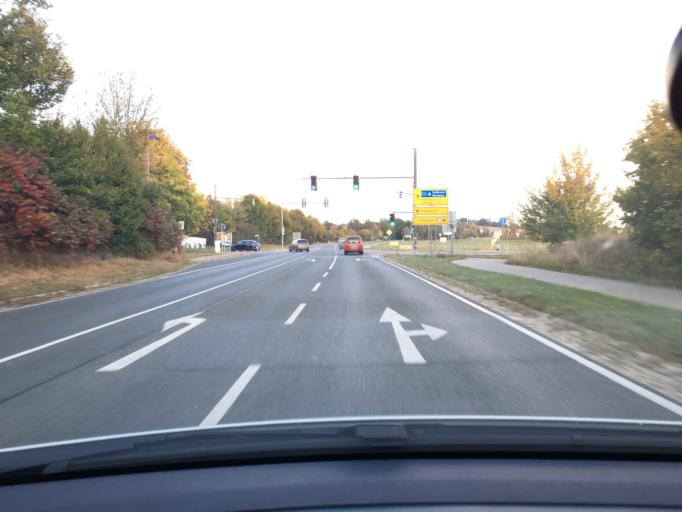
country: DE
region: Bavaria
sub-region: Regierungsbezirk Mittelfranken
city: Sachsen
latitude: 49.2842
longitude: 10.6584
